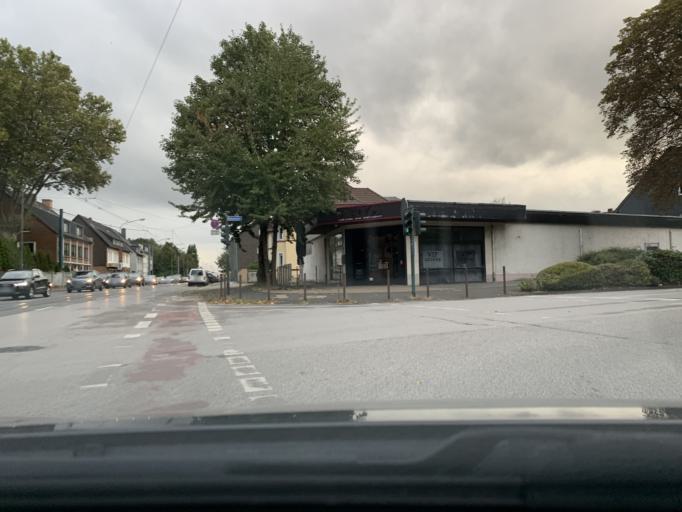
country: DE
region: North Rhine-Westphalia
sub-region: Regierungsbezirk Dusseldorf
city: Oberhausen
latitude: 51.4648
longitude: 6.9296
